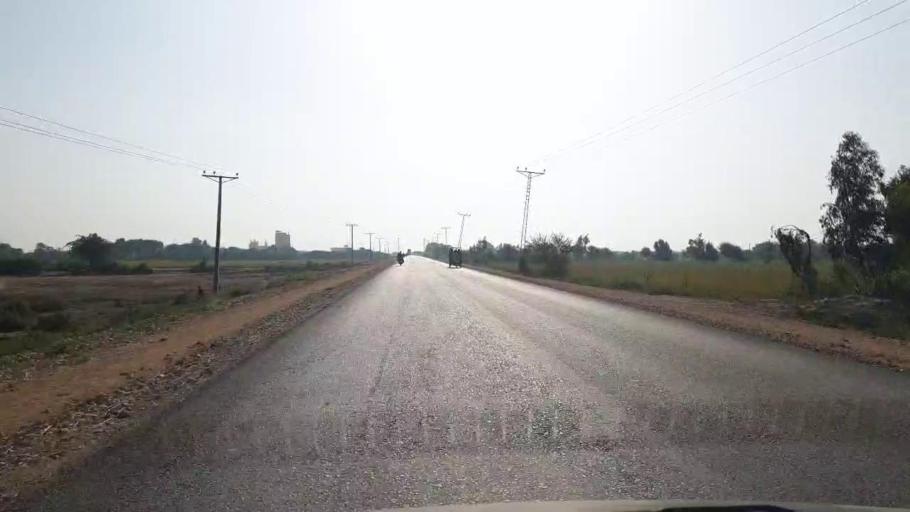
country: PK
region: Sindh
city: Badin
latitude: 24.6635
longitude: 68.8738
